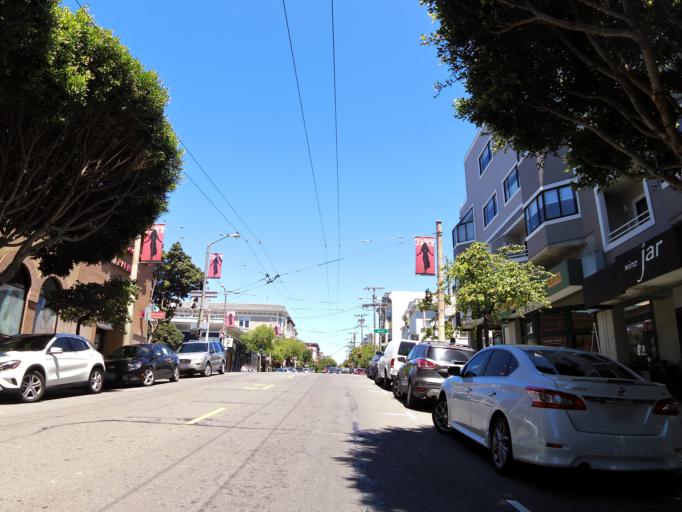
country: US
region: California
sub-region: San Francisco County
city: San Francisco
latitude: 37.7866
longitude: -122.4334
